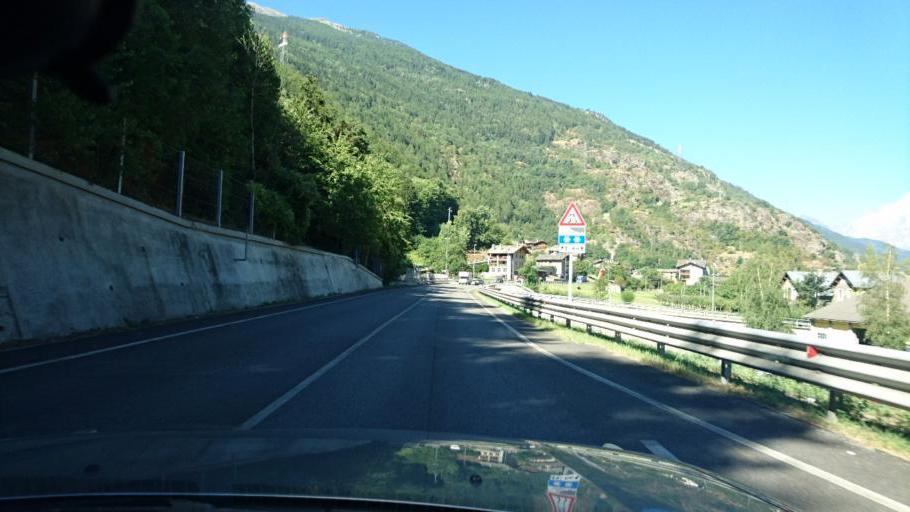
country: IT
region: Aosta Valley
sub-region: Valle d'Aosta
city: Avise
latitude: 45.7052
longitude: 7.1323
